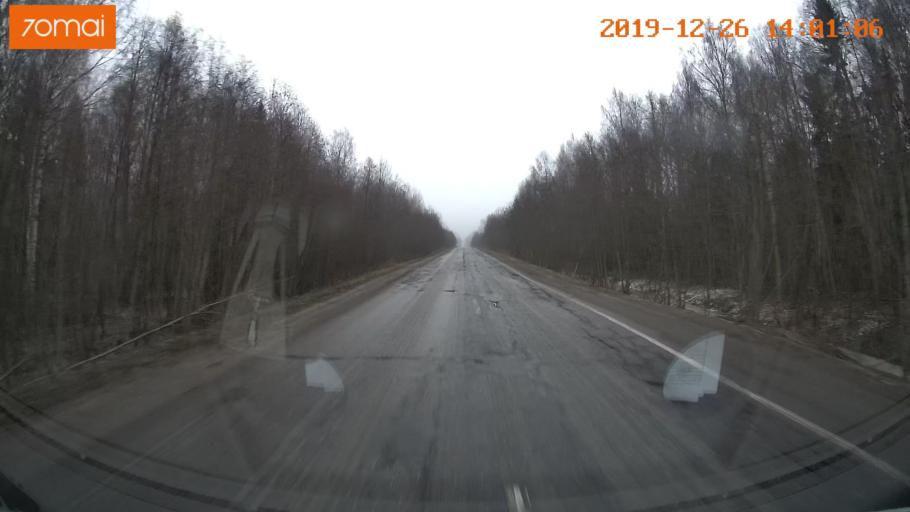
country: RU
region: Jaroslavl
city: Poshekhon'ye
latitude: 58.5529
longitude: 38.7573
